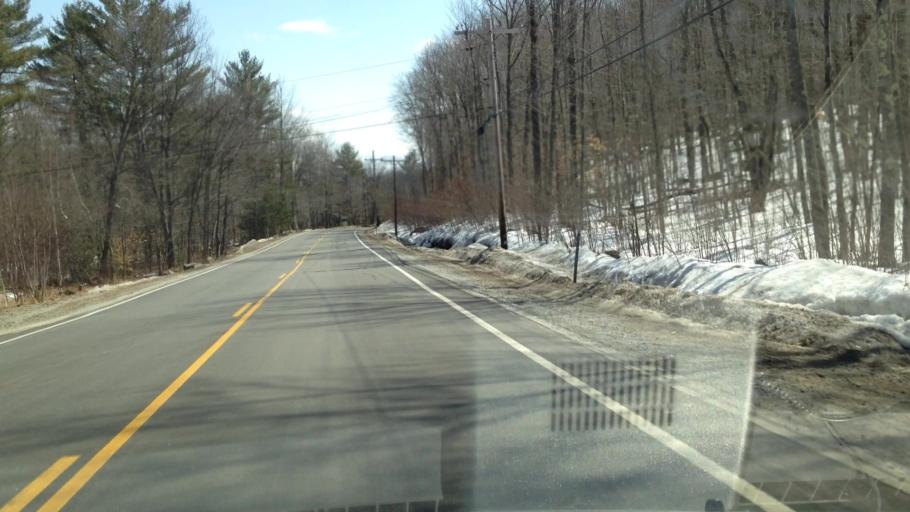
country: US
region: New Hampshire
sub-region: Merrimack County
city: Wilmot
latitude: 43.4622
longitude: -71.9454
